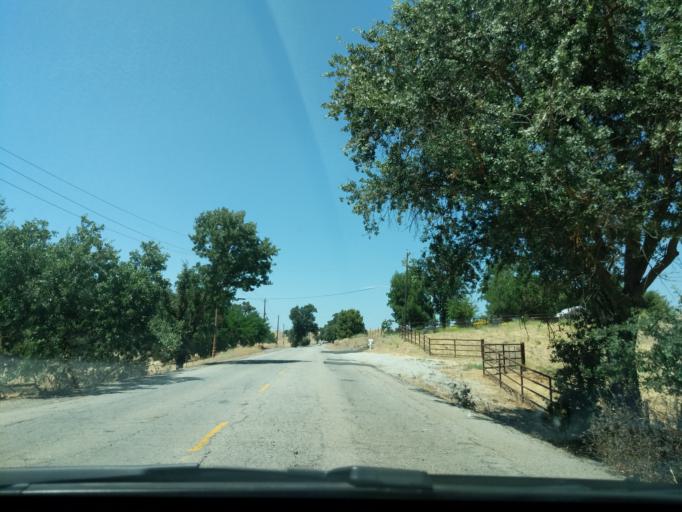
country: US
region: California
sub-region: San Luis Obispo County
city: Paso Robles
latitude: 35.6537
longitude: -120.6407
